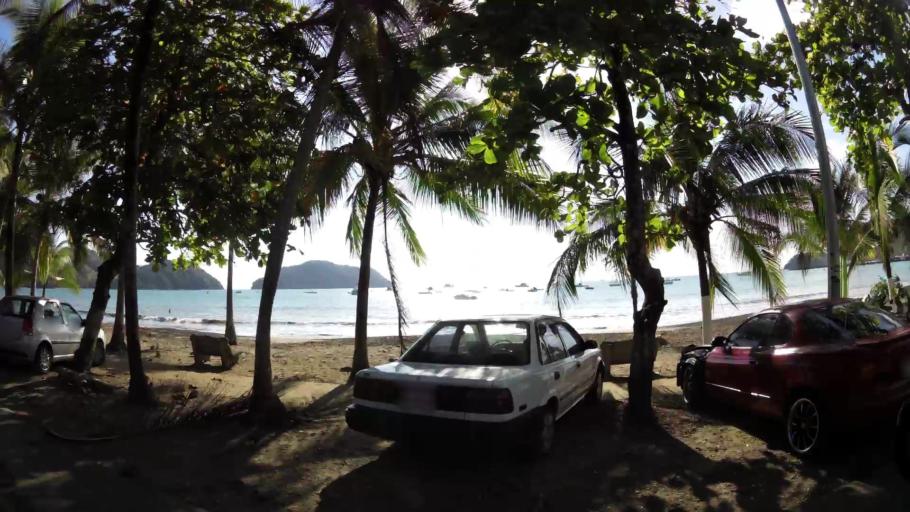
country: CR
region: Puntarenas
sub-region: Canton de Garabito
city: Jaco
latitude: 9.6476
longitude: -84.6563
